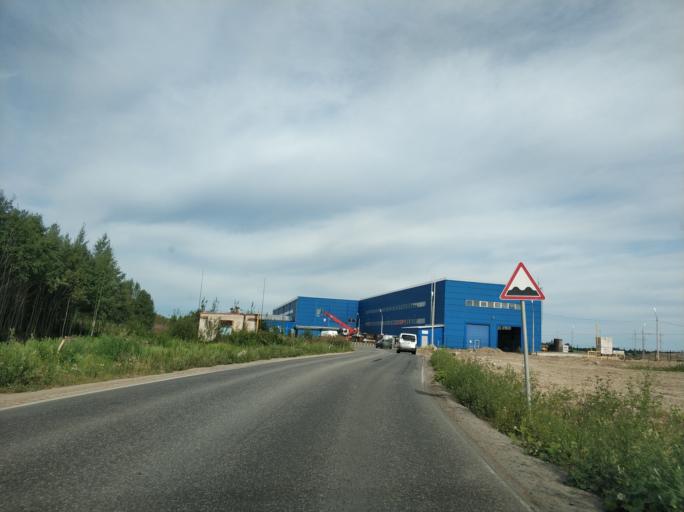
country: RU
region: St.-Petersburg
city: Grazhdanka
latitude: 60.0476
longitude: 30.4126
